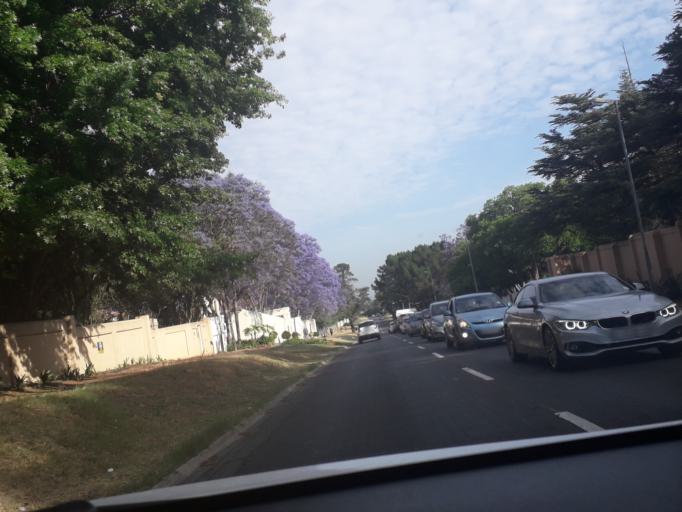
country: ZA
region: Gauteng
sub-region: City of Johannesburg Metropolitan Municipality
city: Johannesburg
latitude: -26.0749
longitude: 28.0083
